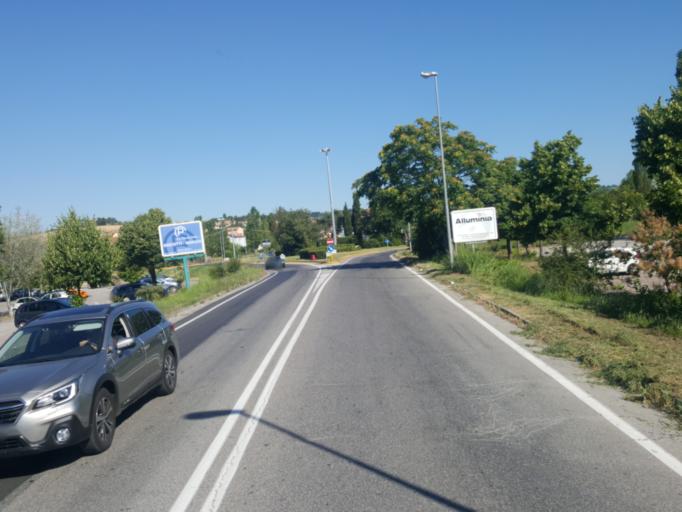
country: IT
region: The Marches
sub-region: Provincia di Pesaro e Urbino
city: Borgo Santa Maria
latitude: 43.8713
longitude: 12.8050
